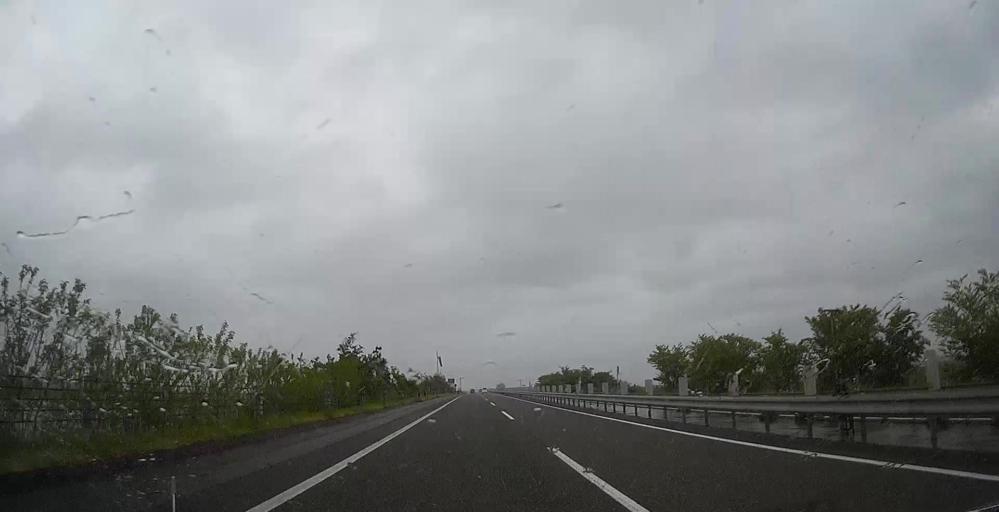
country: JP
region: Niigata
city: Nagaoka
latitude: 37.5011
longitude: 138.8391
